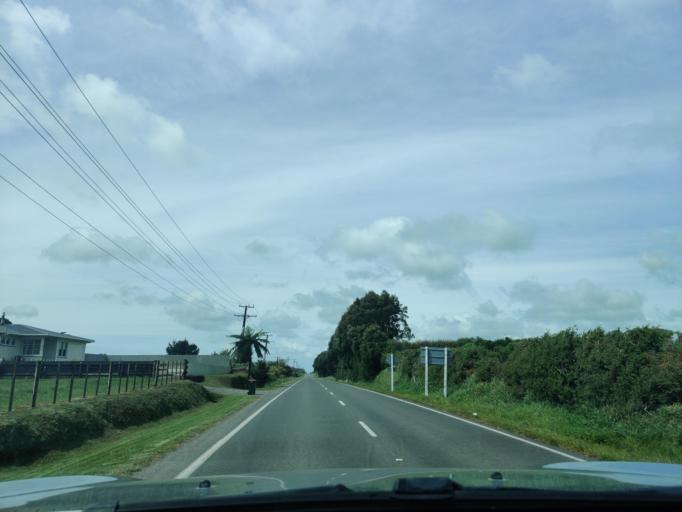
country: NZ
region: Taranaki
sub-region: South Taranaki District
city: Eltham
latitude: -39.4285
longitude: 174.1580
